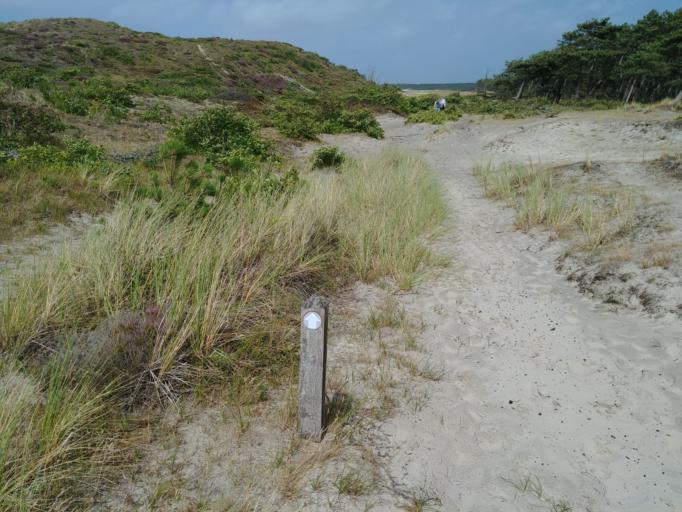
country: NL
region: North Holland
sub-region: Gemeente Bergen
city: Egmond aan Zee
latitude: 52.6853
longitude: 4.6415
